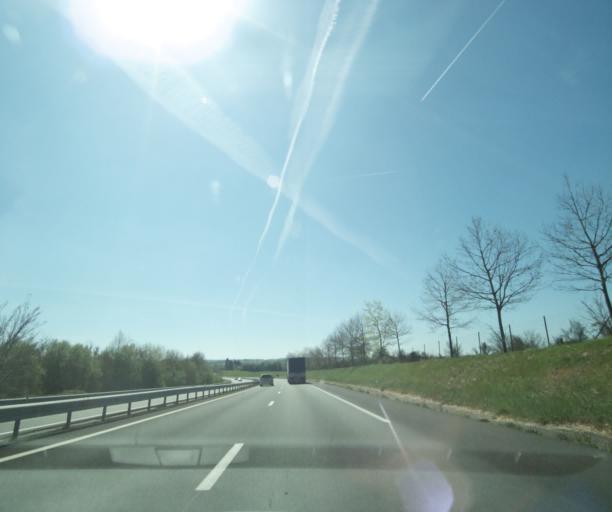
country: FR
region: Limousin
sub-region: Departement de la Haute-Vienne
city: Saint-Sulpice-les-Feuilles
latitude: 46.3004
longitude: 1.4150
